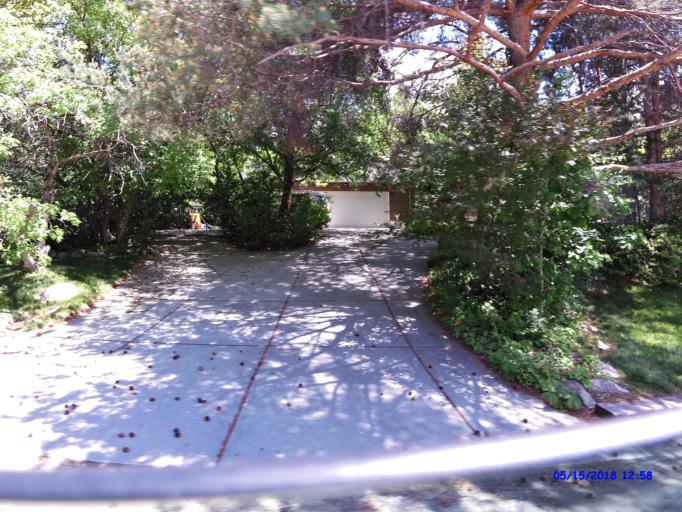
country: US
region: Utah
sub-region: Weber County
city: Uintah
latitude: 41.1614
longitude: -111.9195
